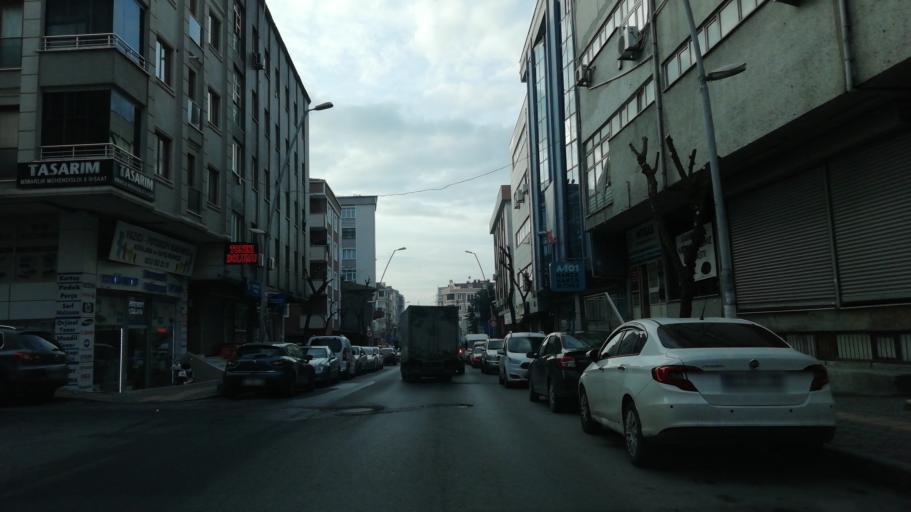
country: TR
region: Istanbul
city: Bahcelievler
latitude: 41.0017
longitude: 28.8269
